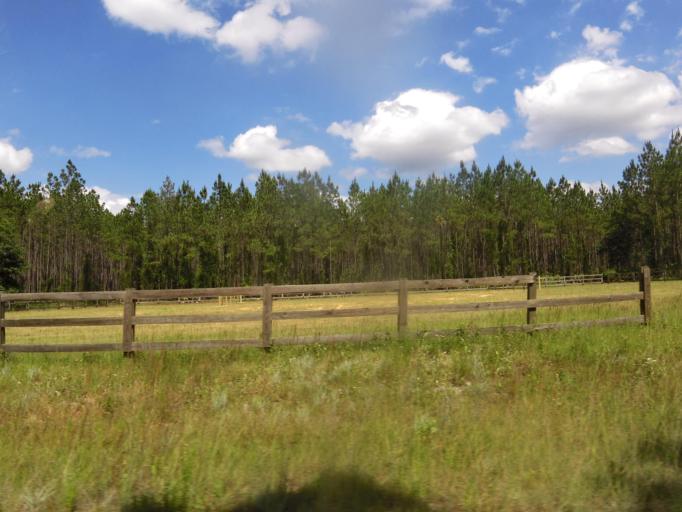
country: US
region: Florida
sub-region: Clay County
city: Asbury Lake
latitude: 29.8728
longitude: -81.8530
